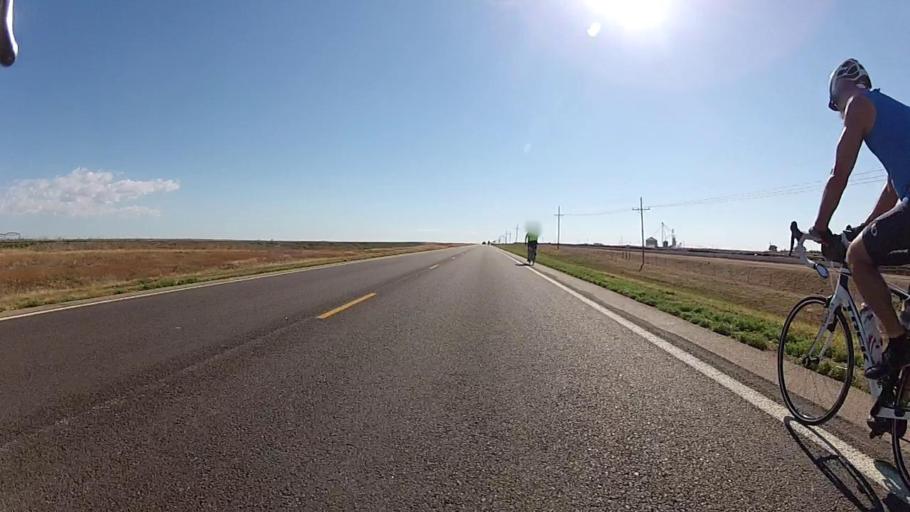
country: US
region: Kansas
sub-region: Gray County
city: Cimarron
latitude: 37.5711
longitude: -100.5385
